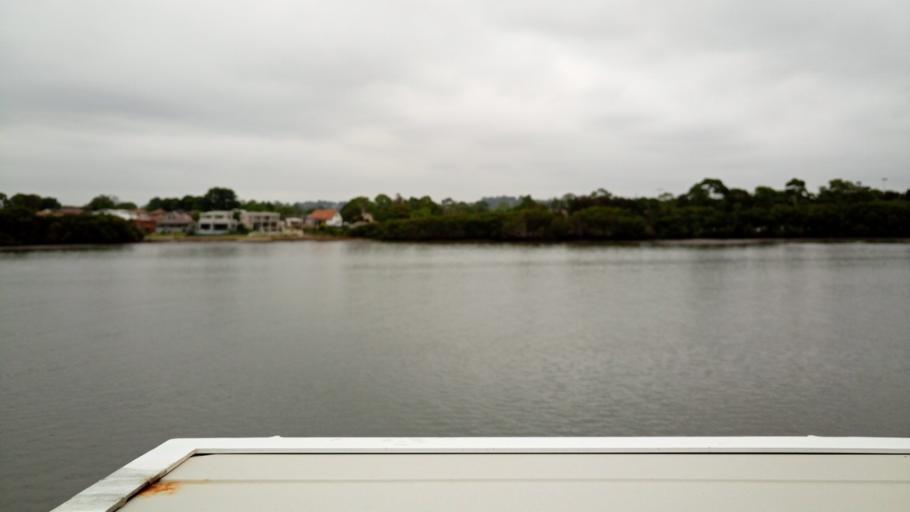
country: AU
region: New South Wales
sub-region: Canada Bay
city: Rhodes
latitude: -33.8215
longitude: 151.0818
